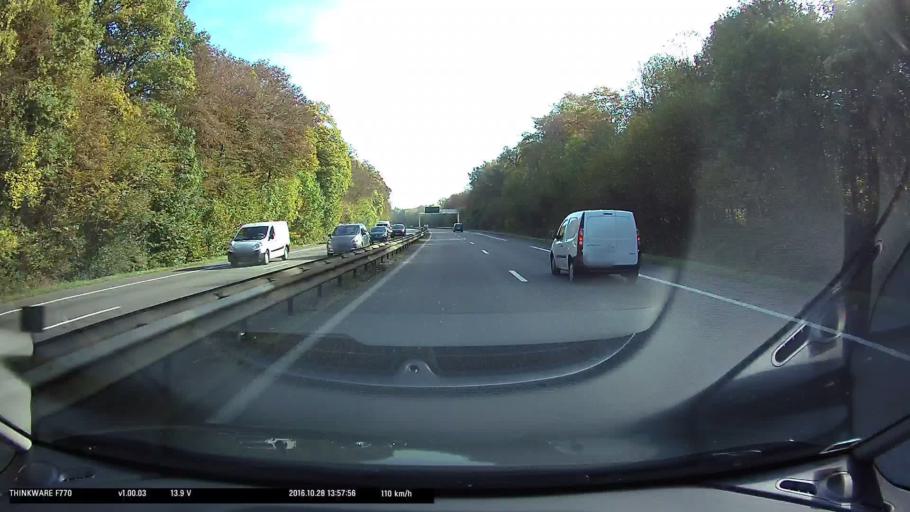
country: FR
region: Lorraine
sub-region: Departement de Meurthe-et-Moselle
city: Chavigny
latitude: 48.6515
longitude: 6.1309
